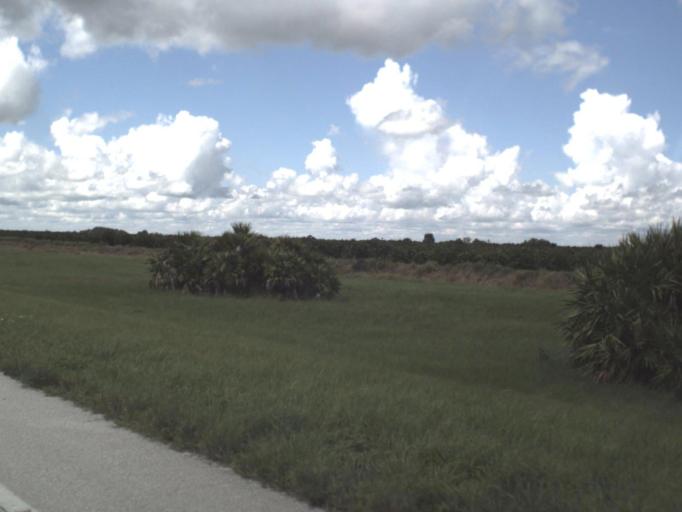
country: US
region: Florida
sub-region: Highlands County
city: Placid Lakes
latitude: 27.2097
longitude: -81.5804
